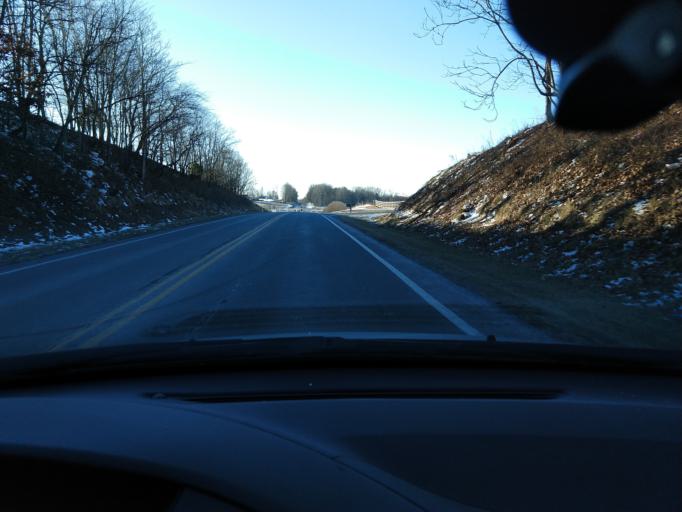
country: US
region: Virginia
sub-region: City of Bedford
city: Bedford
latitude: 37.2800
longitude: -79.5528
